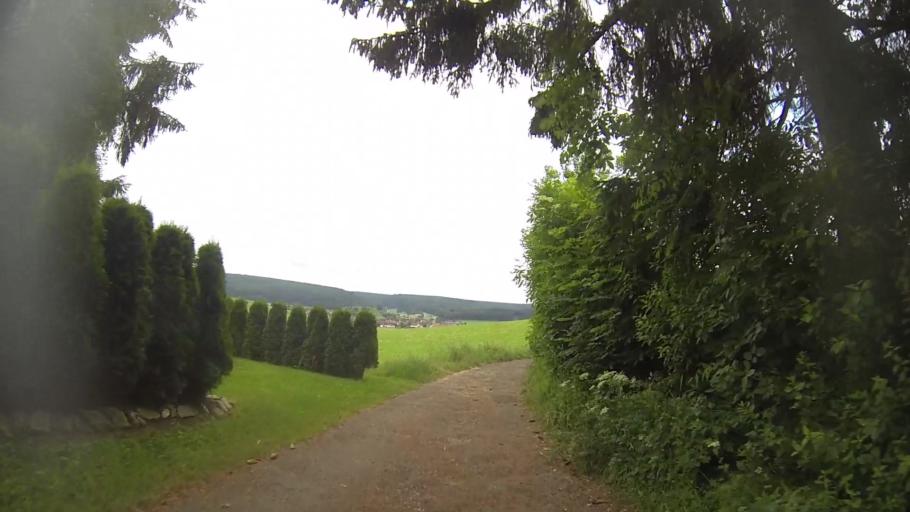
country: DE
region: Baden-Wuerttemberg
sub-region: Regierungsbezirk Stuttgart
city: Steinheim am Albuch
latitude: 48.6866
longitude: 10.0701
